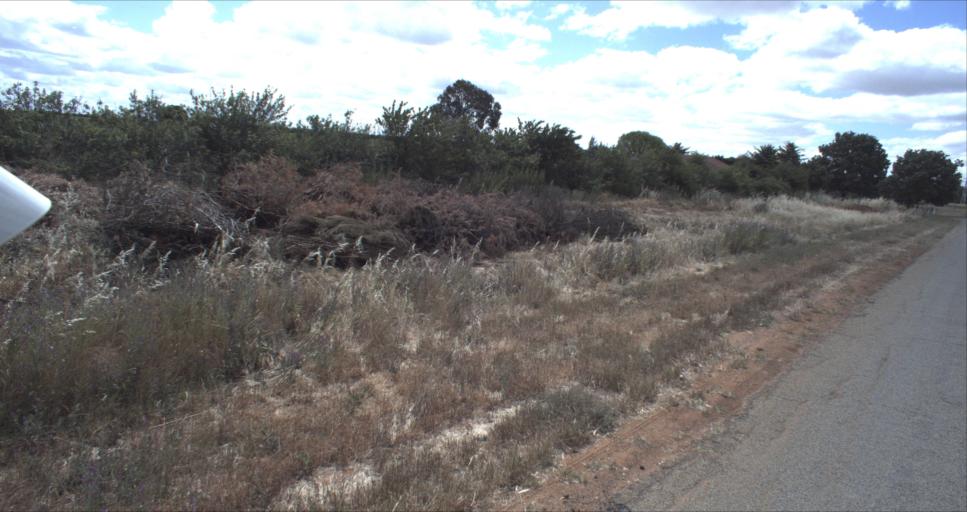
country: AU
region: New South Wales
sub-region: Leeton
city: Leeton
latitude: -34.5862
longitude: 146.3960
